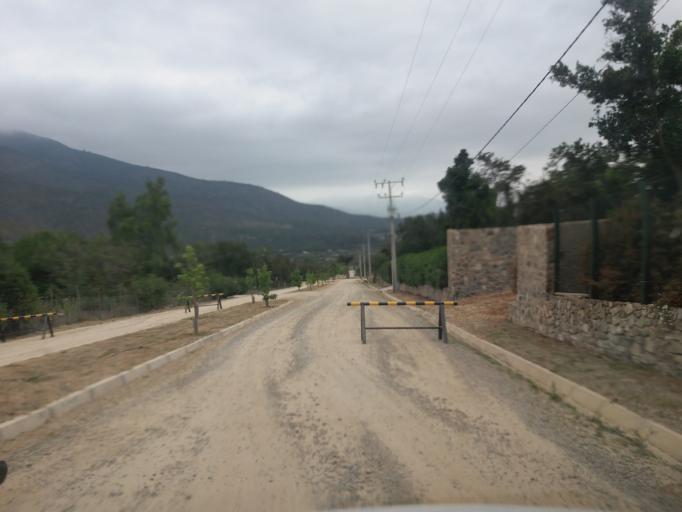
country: CL
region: Valparaiso
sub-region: Provincia de Marga Marga
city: Limache
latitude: -33.0253
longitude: -71.1302
